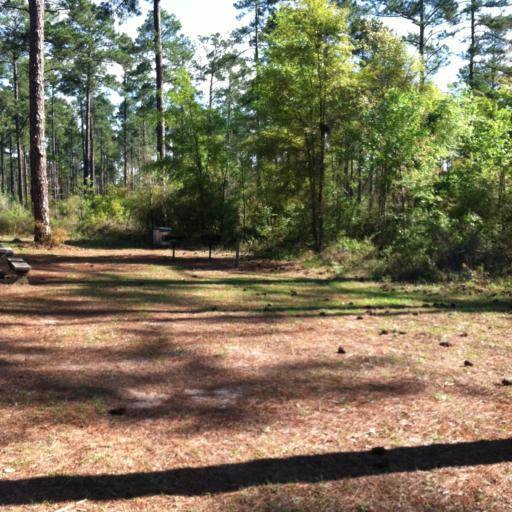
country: US
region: Georgia
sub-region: Early County
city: Blakely
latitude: 31.4710
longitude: -84.9223
